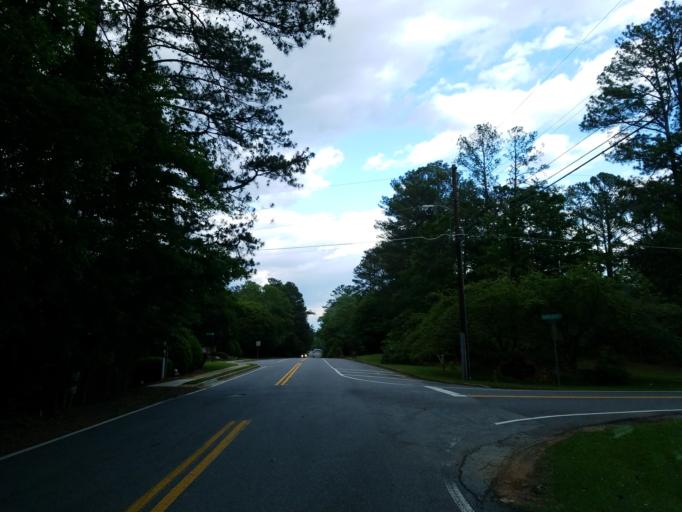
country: US
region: Georgia
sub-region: Fulton County
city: Alpharetta
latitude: 34.0876
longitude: -84.3339
